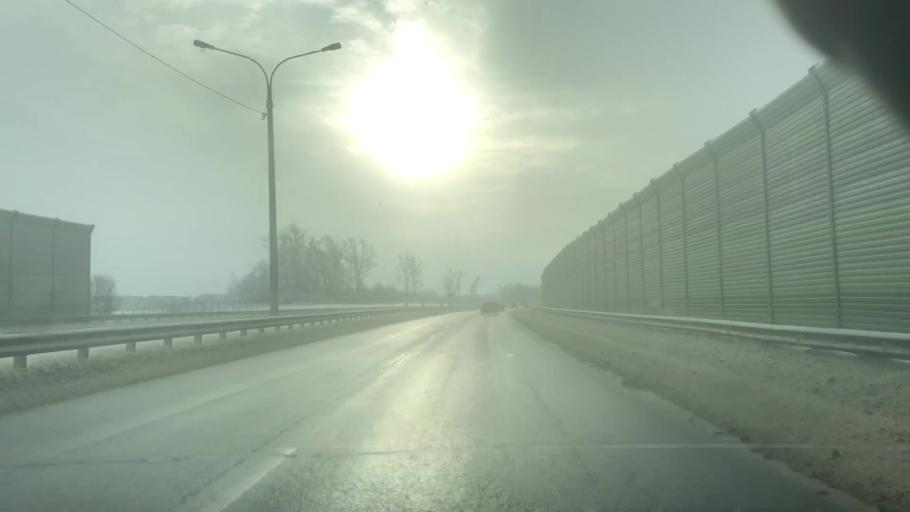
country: RU
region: Tula
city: Venev
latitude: 54.2754
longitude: 38.1605
